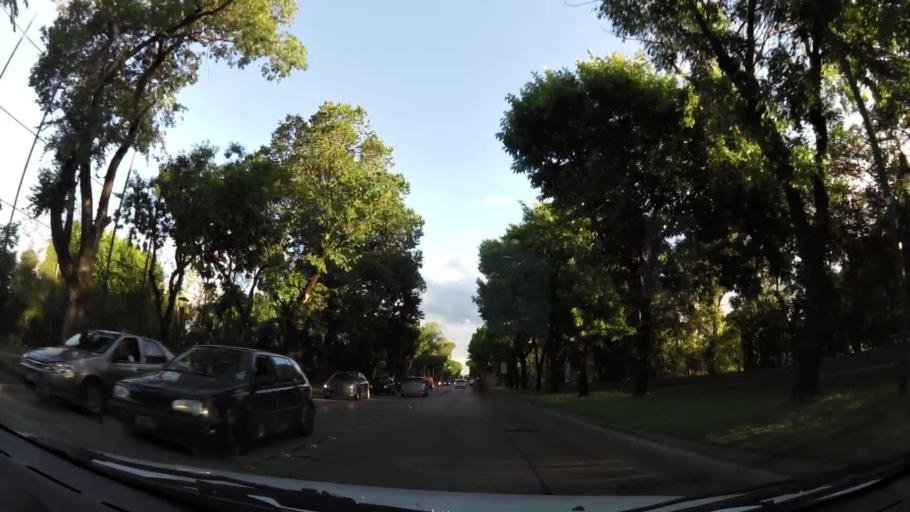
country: AR
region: Buenos Aires
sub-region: Partido de San Isidro
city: San Isidro
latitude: -34.4854
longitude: -58.5265
